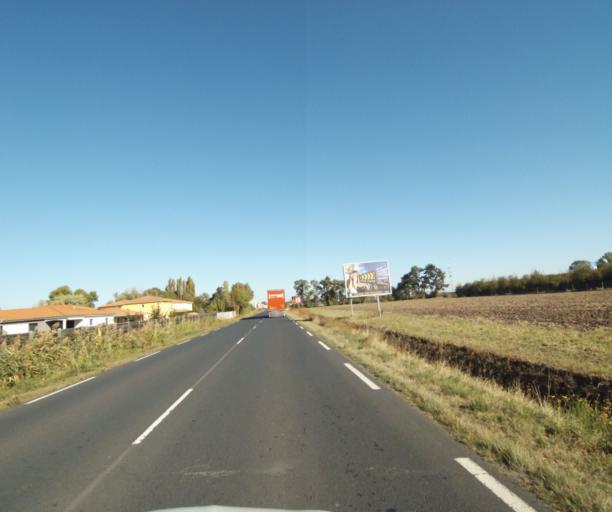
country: FR
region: Auvergne
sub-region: Departement du Puy-de-Dome
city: Gerzat
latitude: 45.8350
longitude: 3.1584
